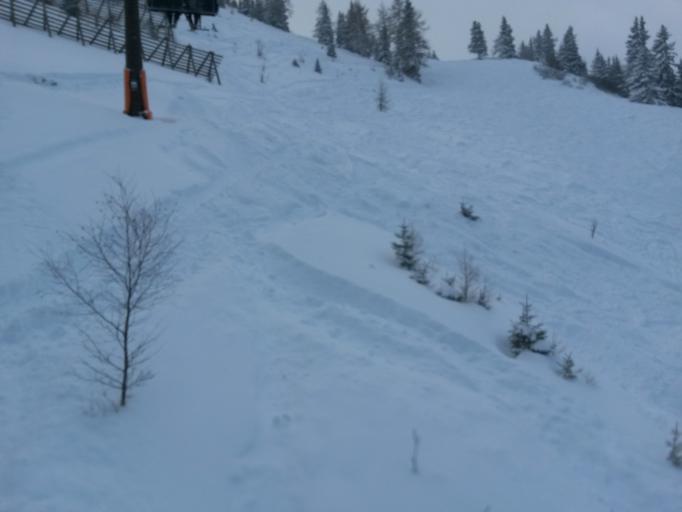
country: AT
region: Salzburg
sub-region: Politischer Bezirk Sankt Johann im Pongau
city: Dorfgastein
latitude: 47.2299
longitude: 13.1655
